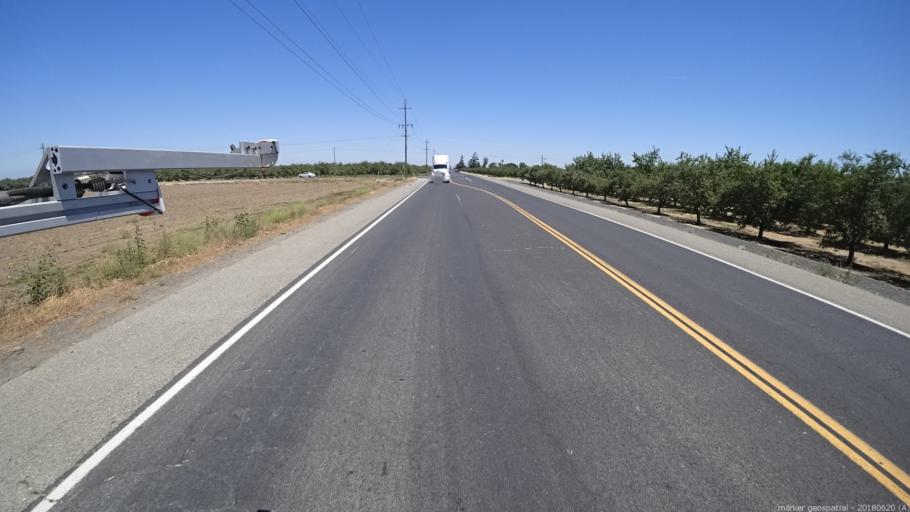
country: US
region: California
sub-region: Madera County
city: Parkwood
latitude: 36.9239
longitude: -120.0751
